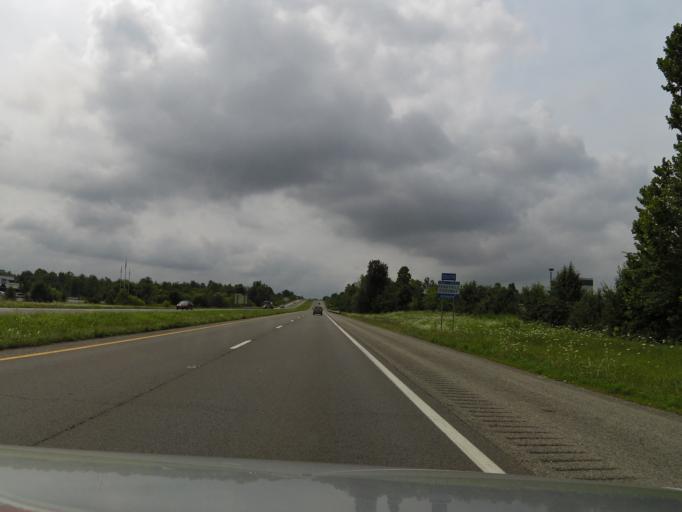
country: US
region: Kentucky
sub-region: Hopkins County
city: Madisonville
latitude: 37.3472
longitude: -87.4835
